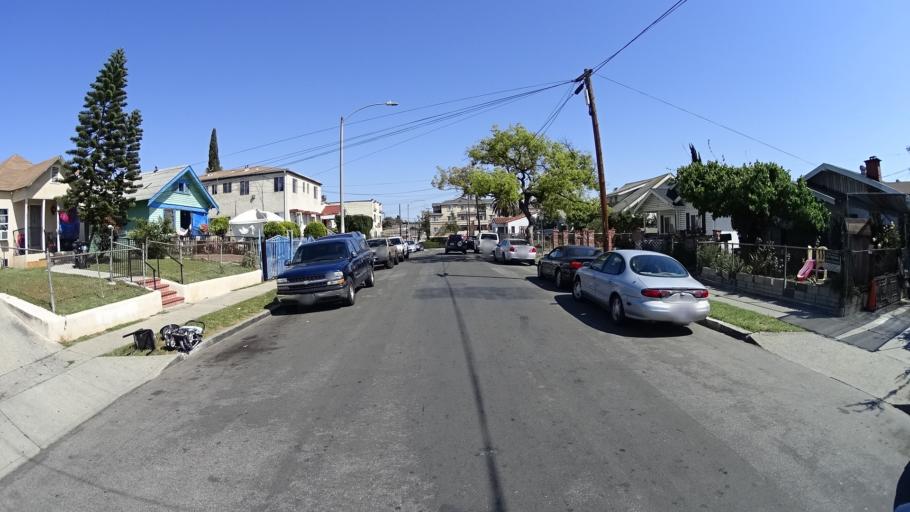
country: US
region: California
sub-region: Los Angeles County
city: Boyle Heights
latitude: 34.0448
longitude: -118.2008
